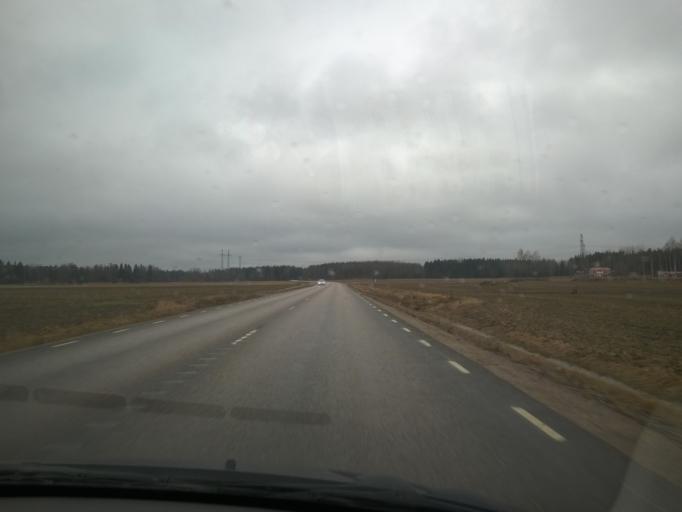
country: SE
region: Uppsala
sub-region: Tierps Kommun
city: Orbyhus
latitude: 60.1765
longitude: 17.5899
